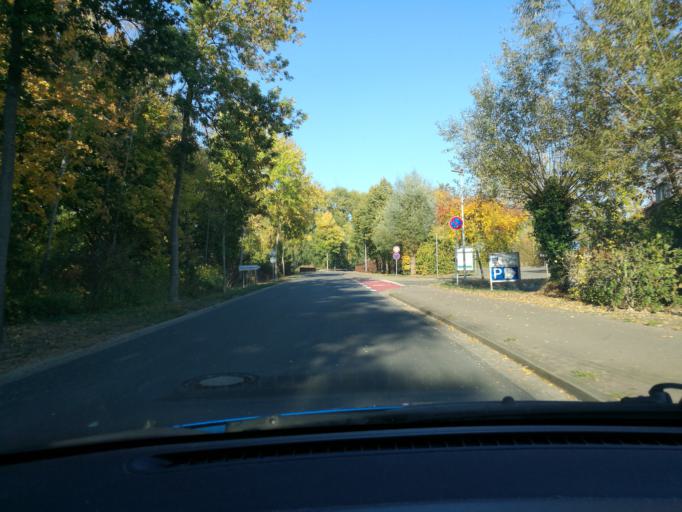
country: DE
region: Lower Saxony
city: Dannenberg
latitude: 53.0994
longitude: 11.0940
